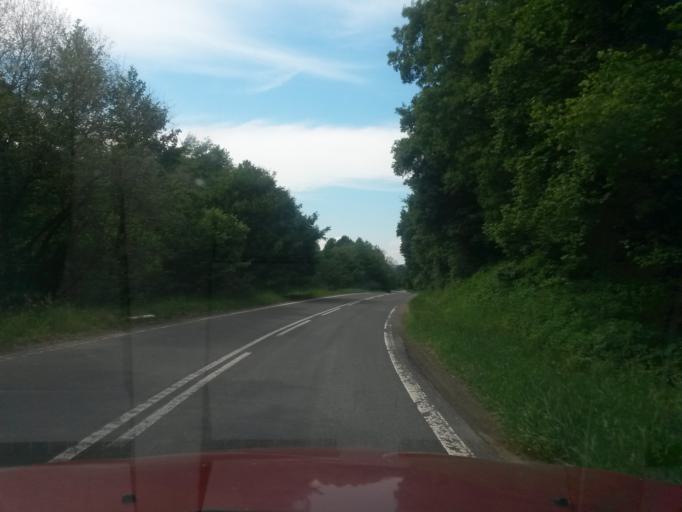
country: SK
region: Presovsky
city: Snina
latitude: 48.9900
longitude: 22.2419
